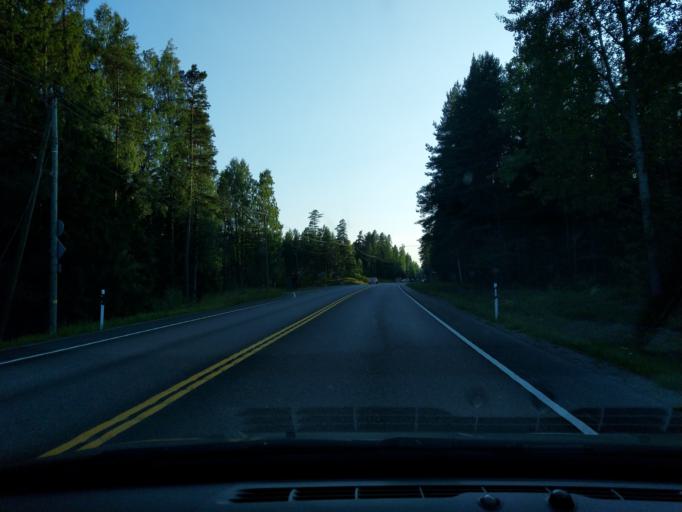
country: FI
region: Uusimaa
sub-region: Helsinki
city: Jaervenpaeae
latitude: 60.6179
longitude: 25.1052
